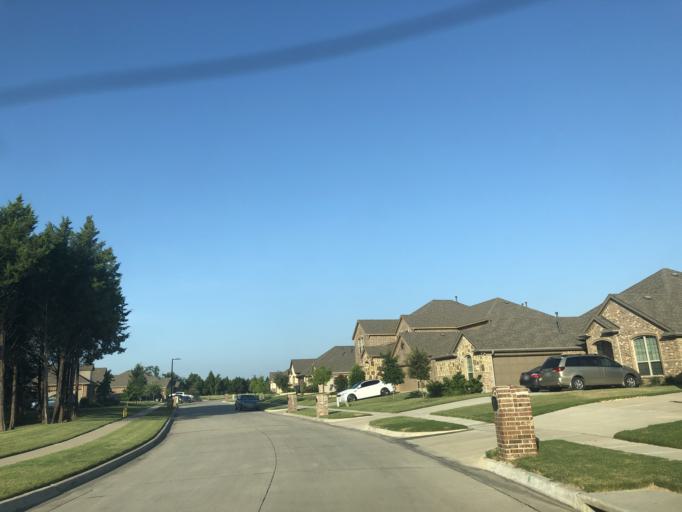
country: US
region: Texas
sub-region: Dallas County
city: Sunnyvale
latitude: 32.8424
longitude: -96.5566
